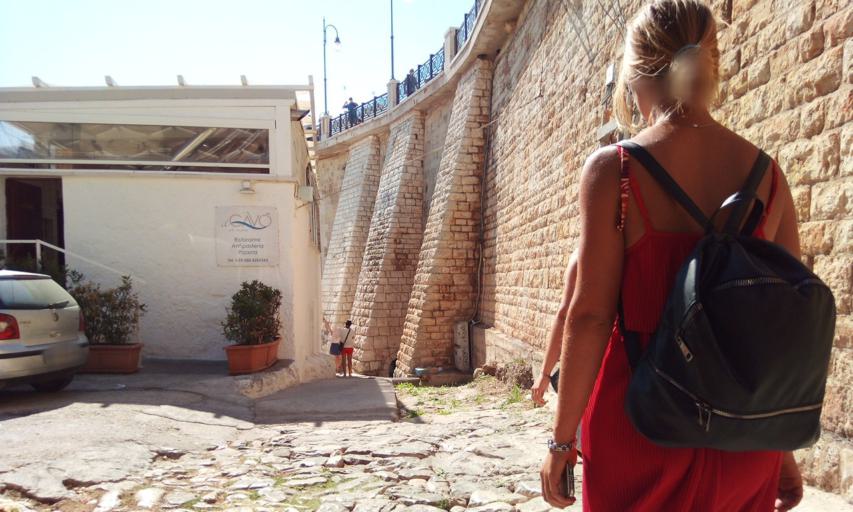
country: IT
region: Apulia
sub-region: Provincia di Bari
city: Polignano a Mare
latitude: 40.9959
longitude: 17.2175
